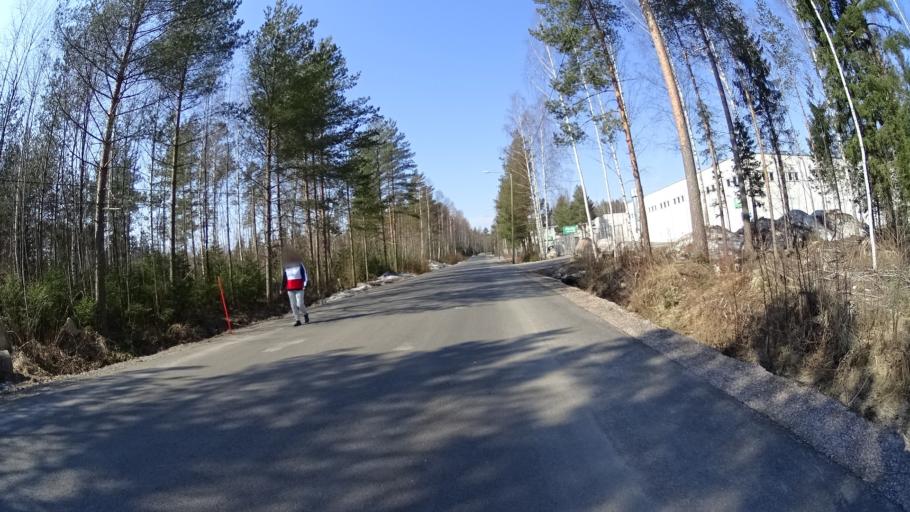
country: FI
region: Uusimaa
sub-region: Helsinki
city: Kirkkonummi
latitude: 60.2691
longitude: 24.4555
